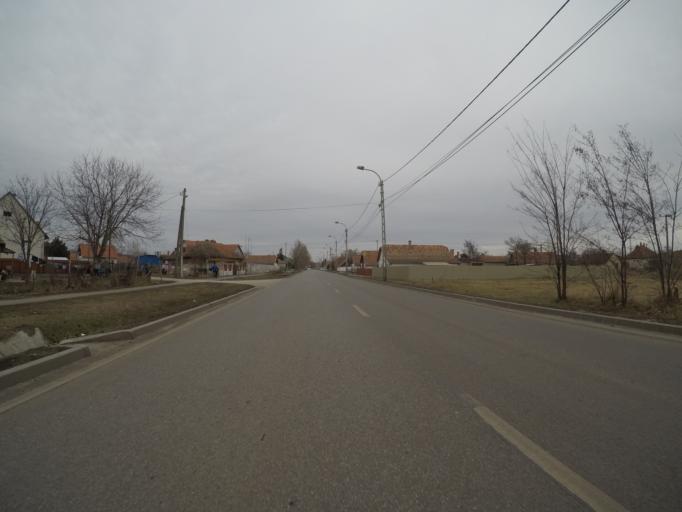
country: HU
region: Jasz-Nagykun-Szolnok
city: Jaszapati
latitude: 47.5099
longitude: 20.1288
